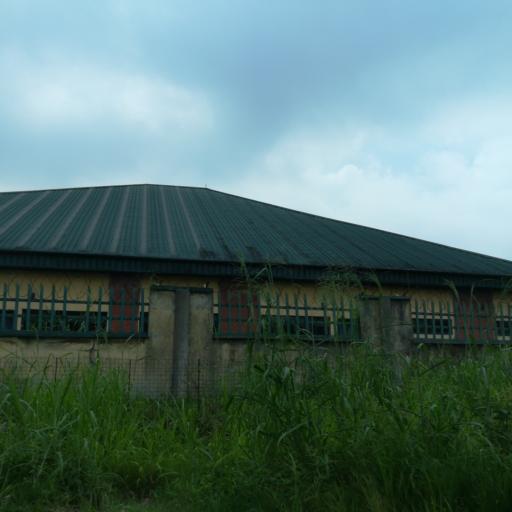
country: NG
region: Rivers
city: Port Harcourt
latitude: 4.8061
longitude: 7.0488
